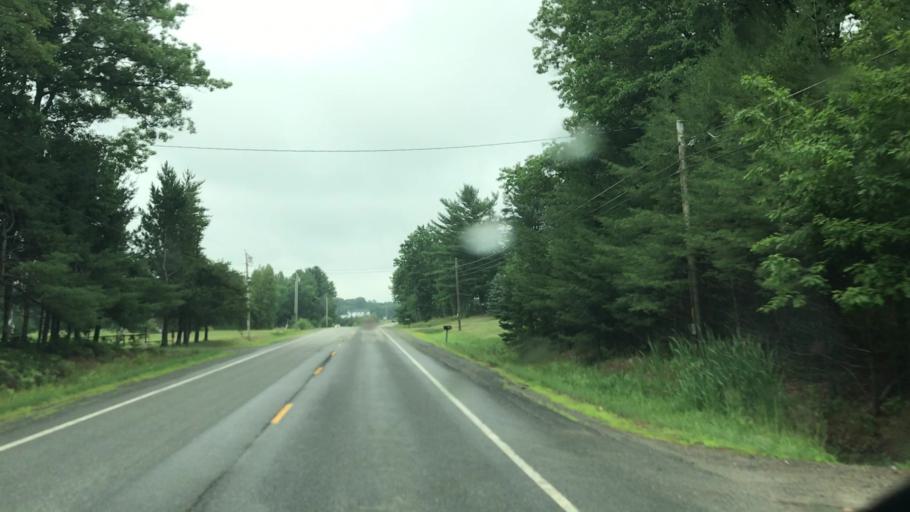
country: US
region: Maine
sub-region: Penobscot County
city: Howland
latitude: 45.2924
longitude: -68.6221
